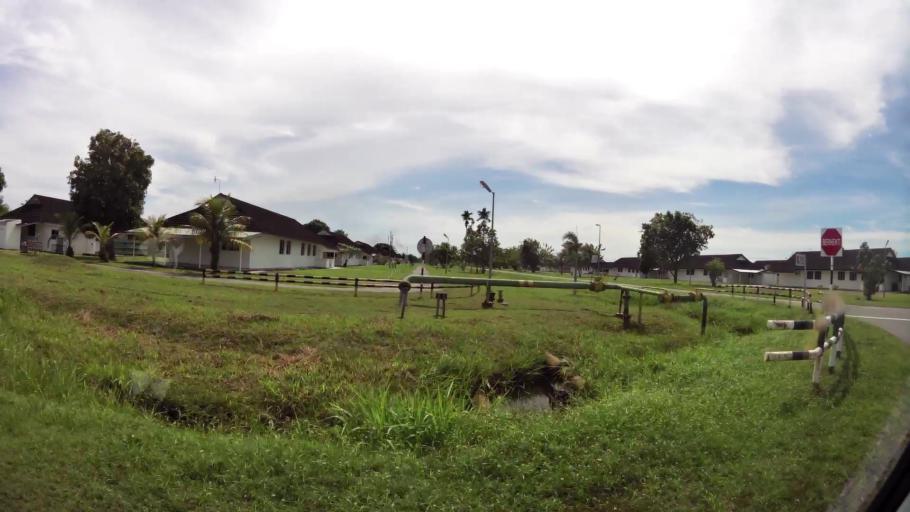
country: BN
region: Belait
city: Seria
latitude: 4.6085
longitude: 114.3199
